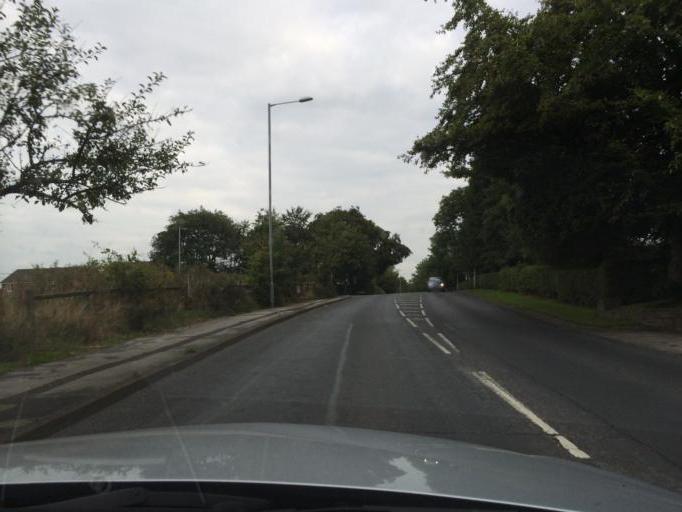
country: GB
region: England
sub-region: Borough of Stockport
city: Hazel Grove
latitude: 53.3875
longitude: -2.1008
